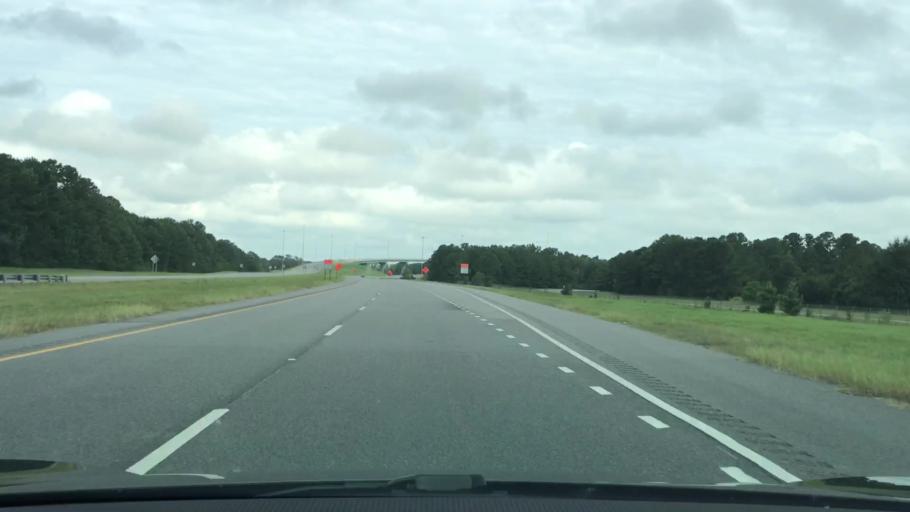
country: US
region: Alabama
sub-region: Montgomery County
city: Pike Road
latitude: 32.3584
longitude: -86.0722
